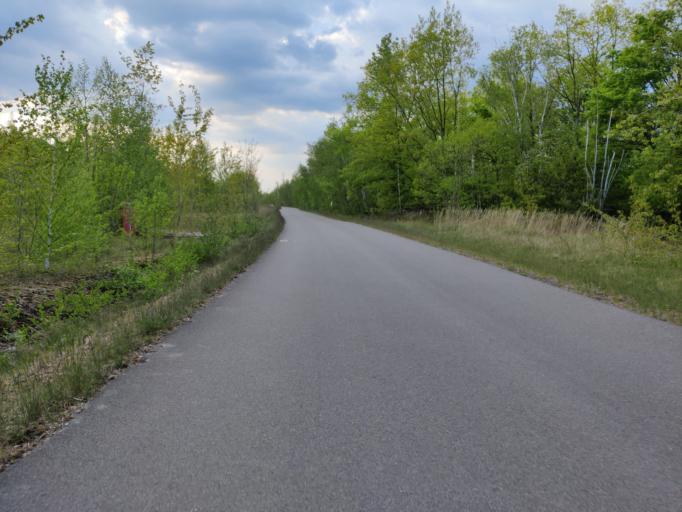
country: DE
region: Saxony
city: Espenhain
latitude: 51.2082
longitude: 12.4459
